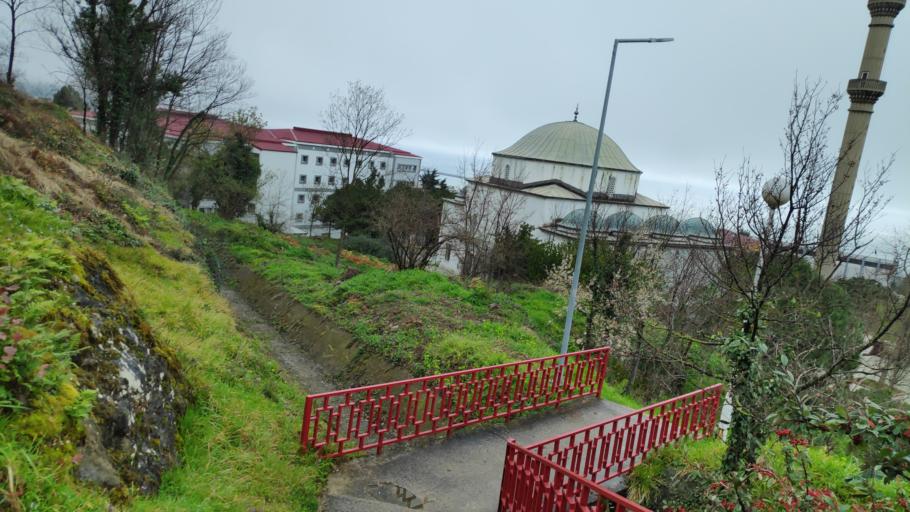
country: TR
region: Trabzon
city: Trabzon
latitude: 40.9947
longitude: 39.7709
